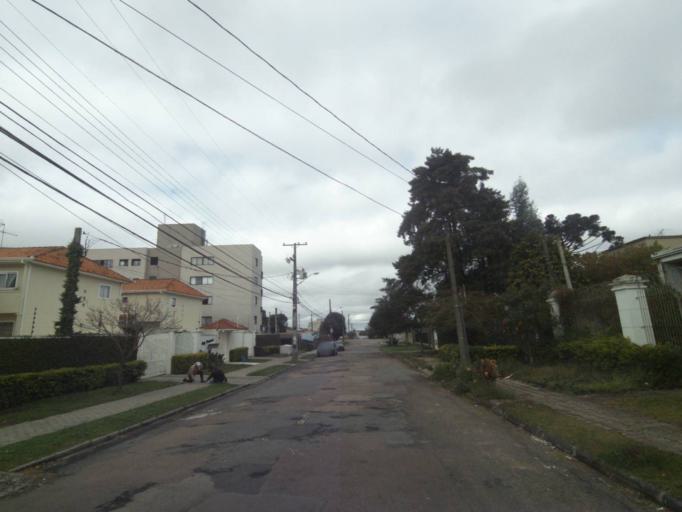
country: BR
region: Parana
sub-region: Curitiba
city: Curitiba
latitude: -25.4981
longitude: -49.2918
